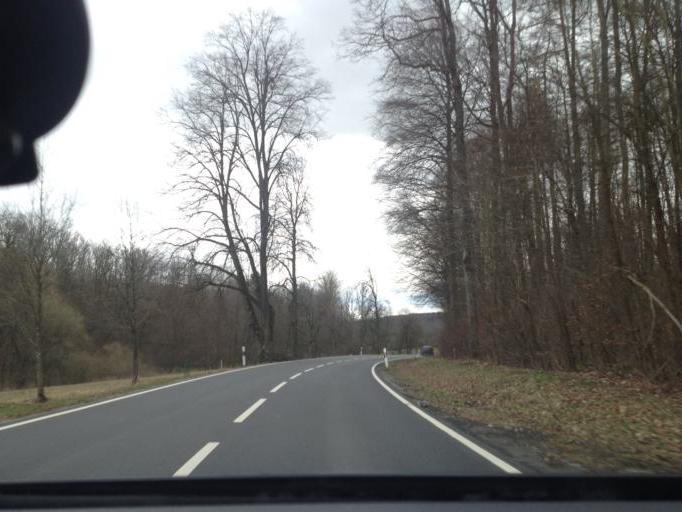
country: DE
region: Bavaria
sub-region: Regierungsbezirk Unterfranken
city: Kist
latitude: 49.7386
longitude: 9.8673
